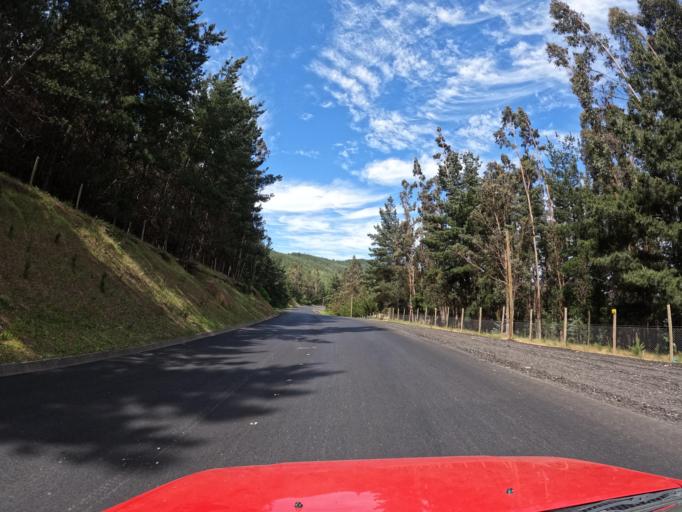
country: CL
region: Maule
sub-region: Provincia de Talca
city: Constitucion
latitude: -35.0441
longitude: -72.0569
